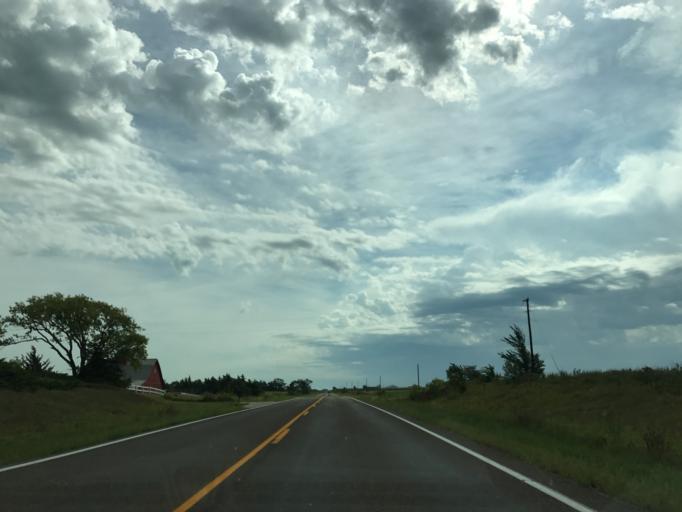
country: US
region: Nebraska
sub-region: Jefferson County
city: Fairbury
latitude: 40.3060
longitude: -97.1675
